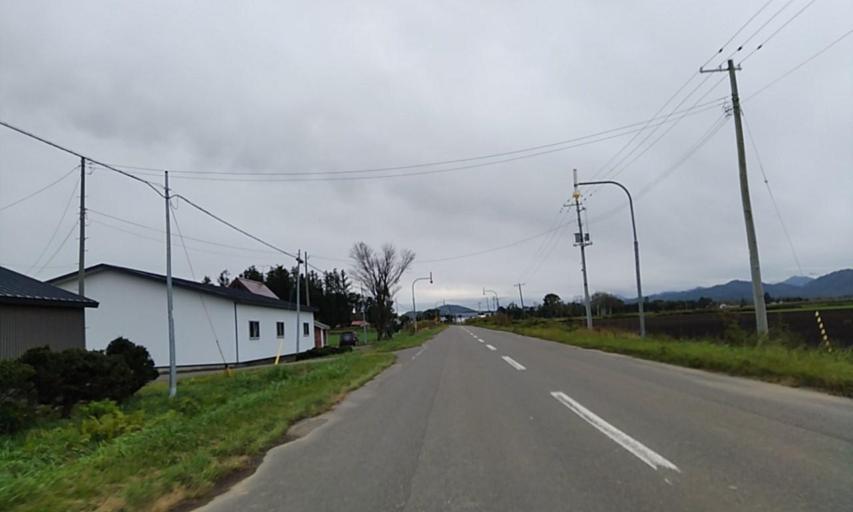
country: JP
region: Hokkaido
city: Obihiro
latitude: 42.6551
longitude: 143.0854
